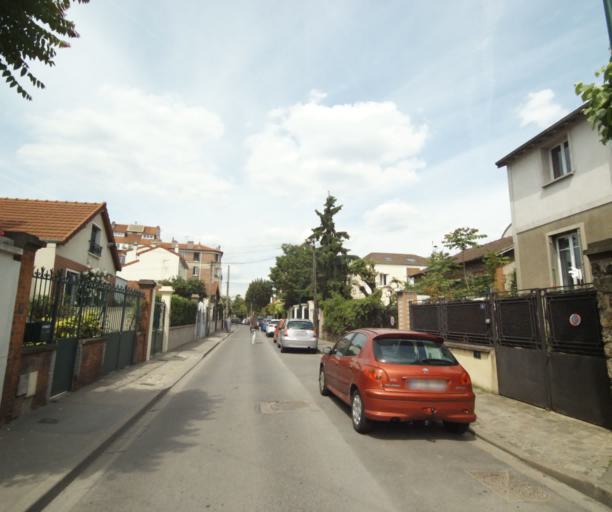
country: FR
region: Ile-de-France
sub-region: Departement des Hauts-de-Seine
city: Bois-Colombes
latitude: 48.9252
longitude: 2.2668
